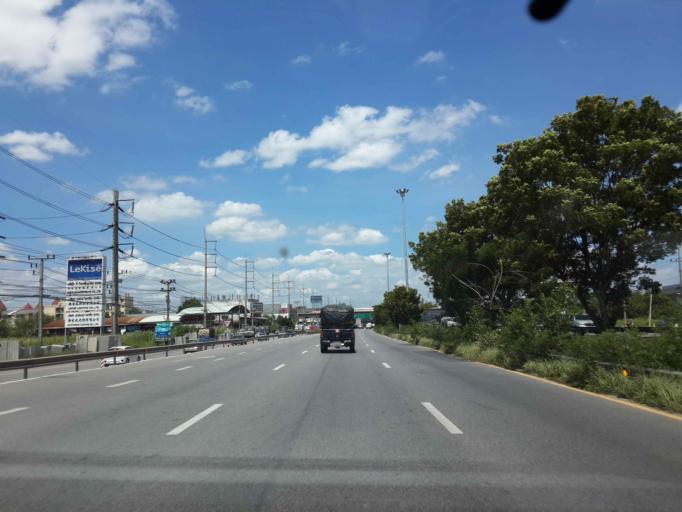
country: TH
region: Samut Sakhon
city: Samut Sakhon
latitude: 13.5847
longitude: 100.3162
